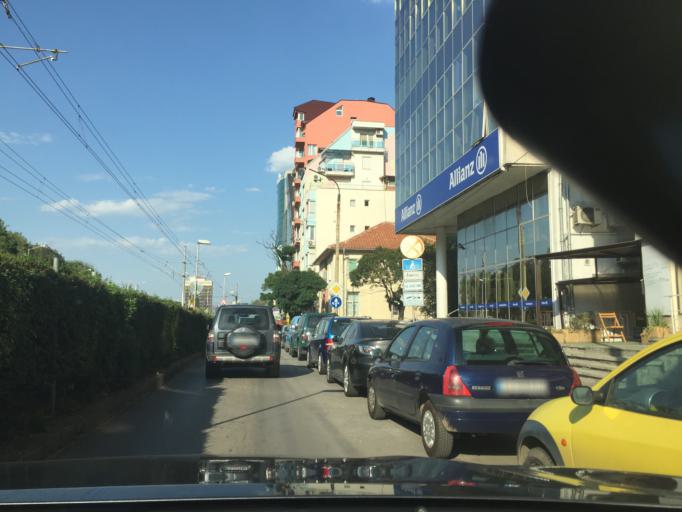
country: BG
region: Sofia-Capital
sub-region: Stolichna Obshtina
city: Sofia
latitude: 42.6857
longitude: 23.2981
